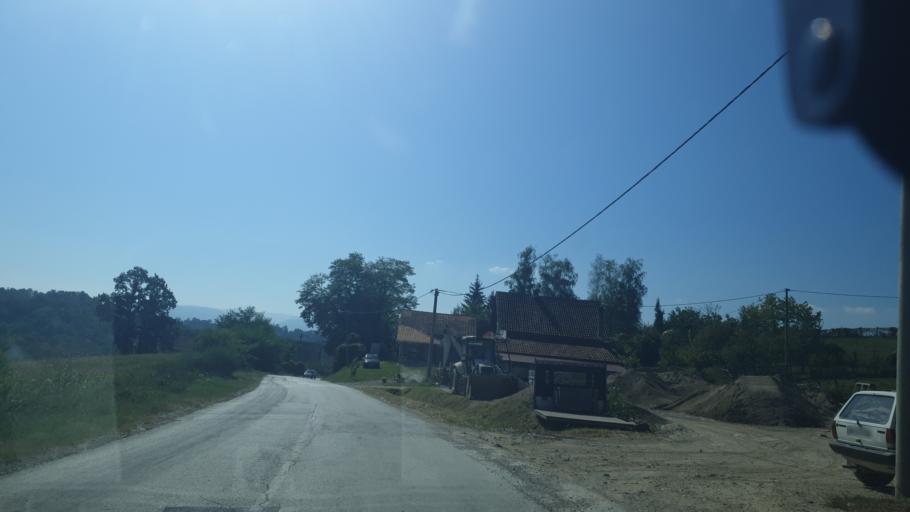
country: RS
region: Central Serbia
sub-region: Kolubarski Okrug
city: Mionica
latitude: 44.2606
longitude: 20.0986
